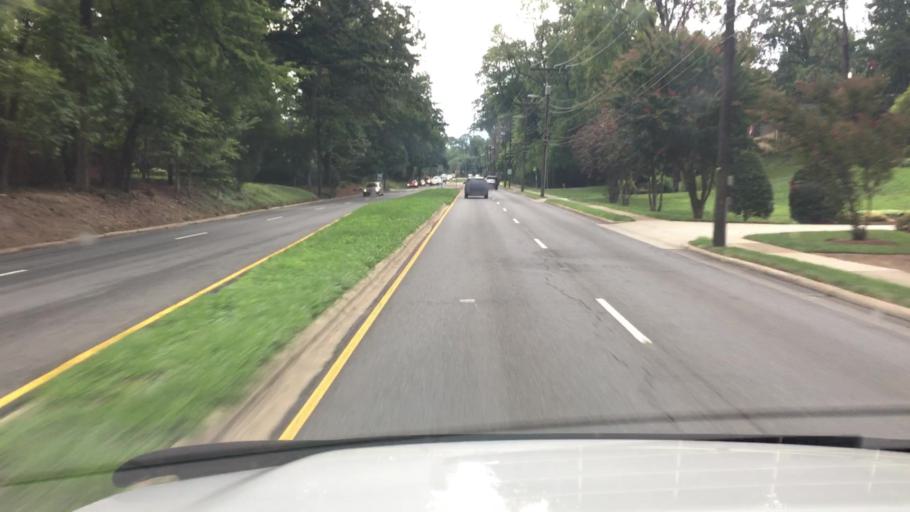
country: US
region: North Carolina
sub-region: Mecklenburg County
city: Charlotte
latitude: 35.1813
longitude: -80.8195
